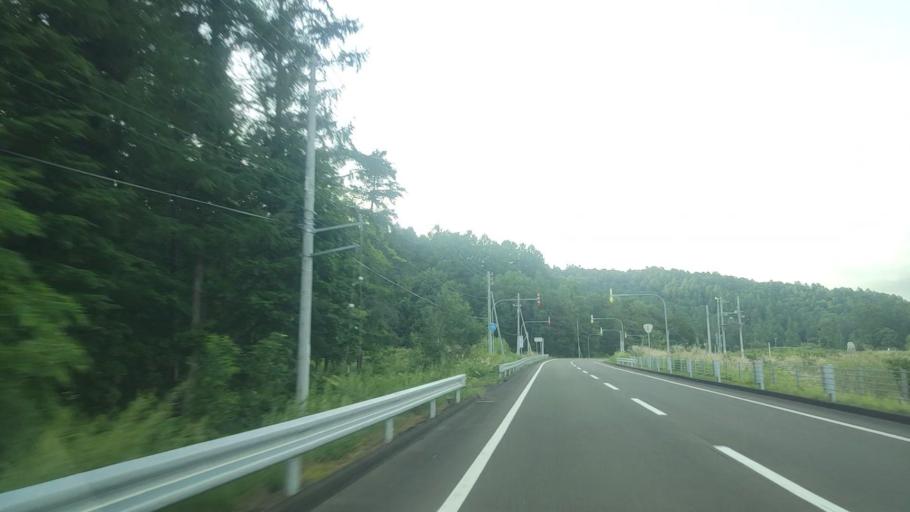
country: JP
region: Hokkaido
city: Bibai
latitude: 43.0616
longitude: 142.0995
